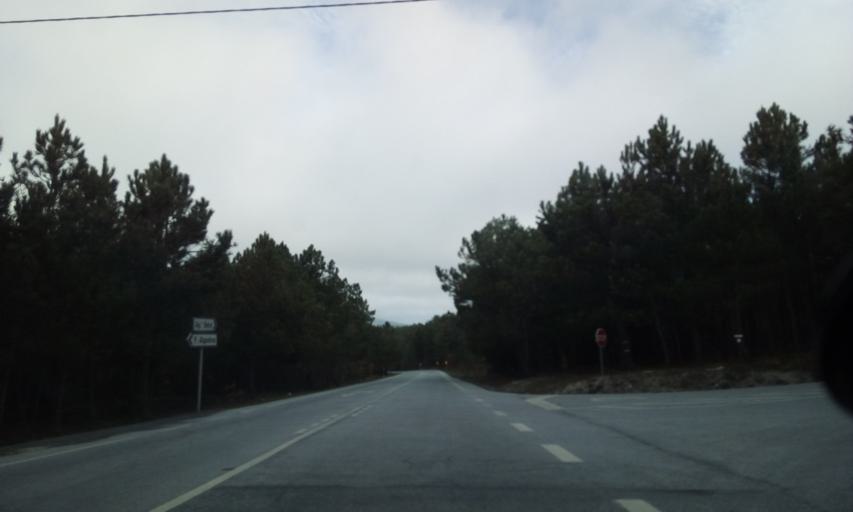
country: PT
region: Guarda
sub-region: Aguiar da Beira
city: Aguiar da Beira
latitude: 40.7993
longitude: -7.5208
